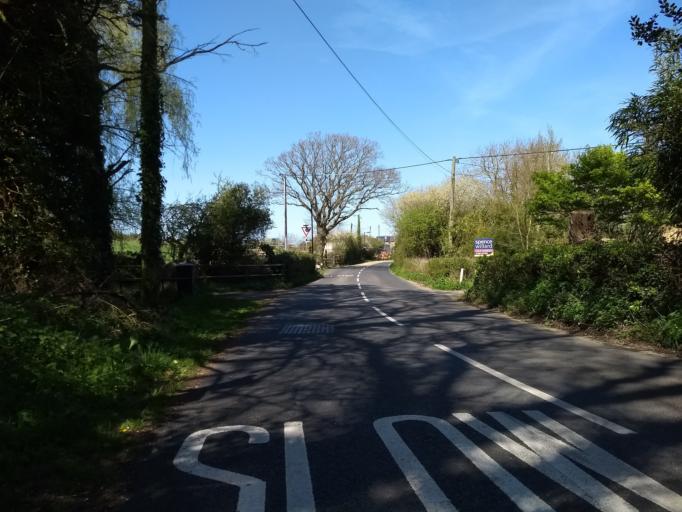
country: GB
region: England
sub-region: Isle of Wight
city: Gurnard
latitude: 50.7545
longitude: -1.3337
